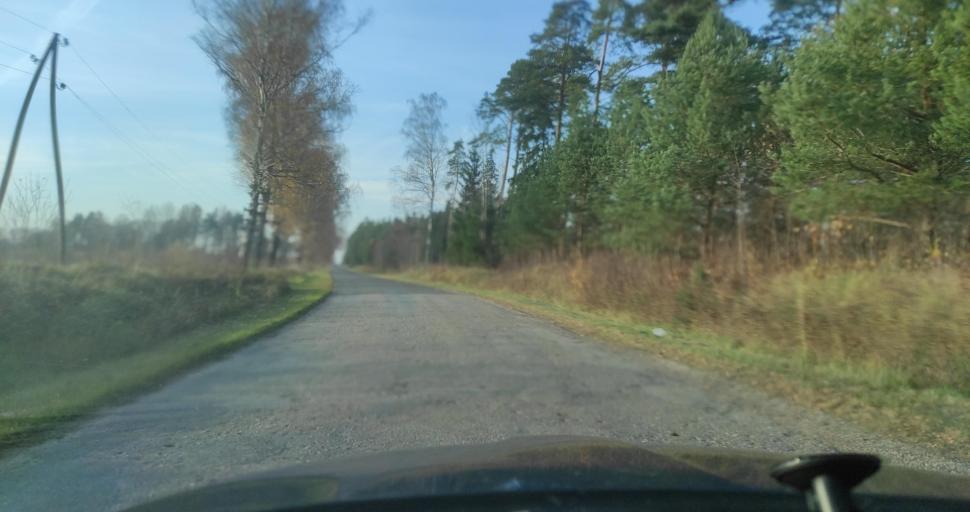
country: LV
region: Skrunda
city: Skrunda
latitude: 56.6826
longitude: 22.0683
